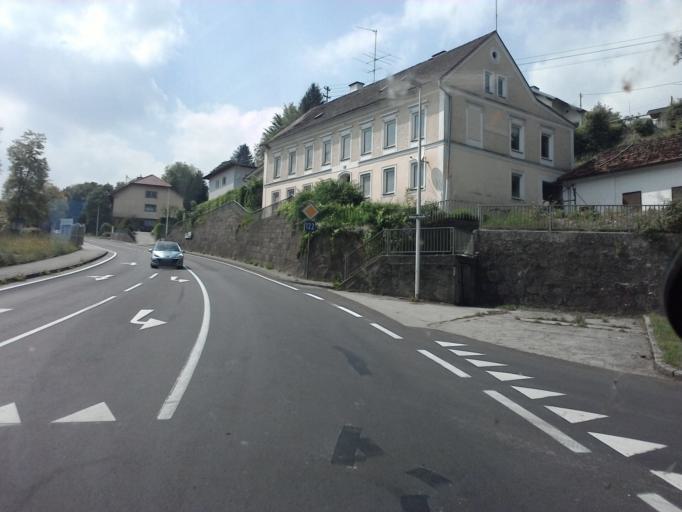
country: AT
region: Upper Austria
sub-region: Politischer Bezirk Kirchdorf an der Krems
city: Kremsmunster
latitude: 48.0547
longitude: 14.1269
